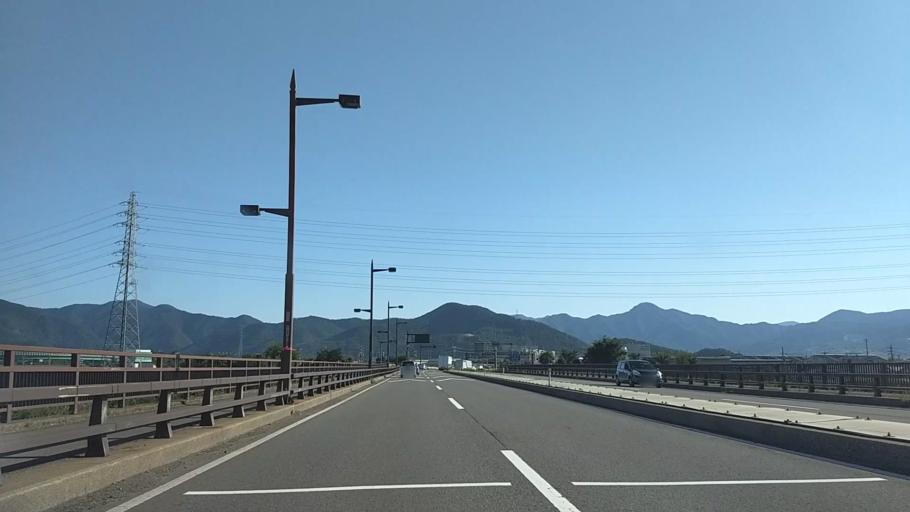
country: JP
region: Nagano
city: Nagano-shi
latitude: 36.5576
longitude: 138.1385
